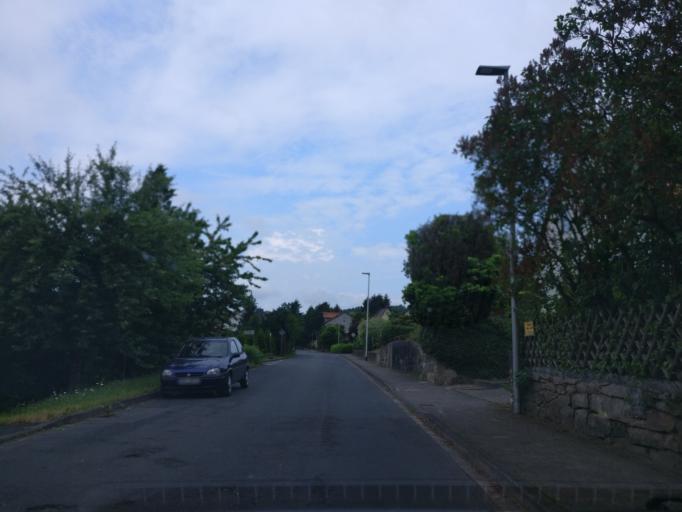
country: DE
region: Lower Saxony
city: Scheden
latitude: 51.4254
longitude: 9.7163
